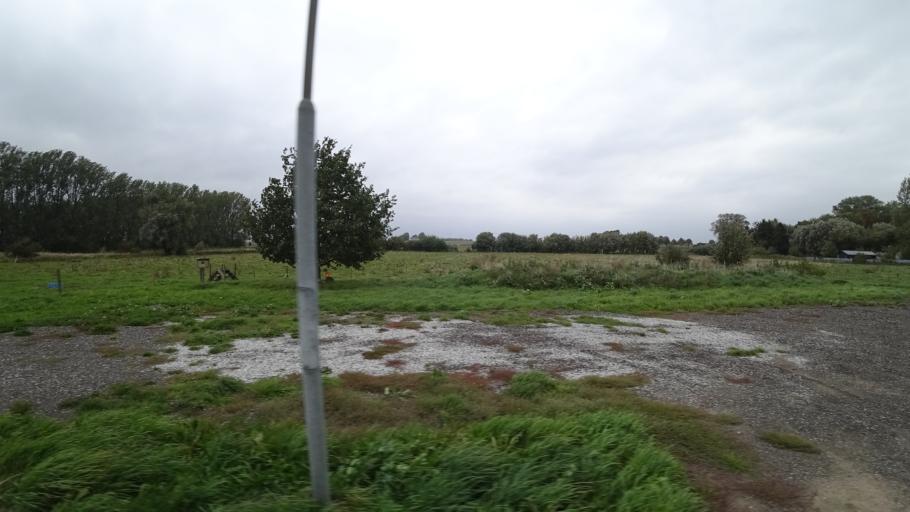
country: SE
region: Skane
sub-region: Kavlinge Kommun
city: Kaevlinge
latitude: 55.7992
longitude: 13.1305
